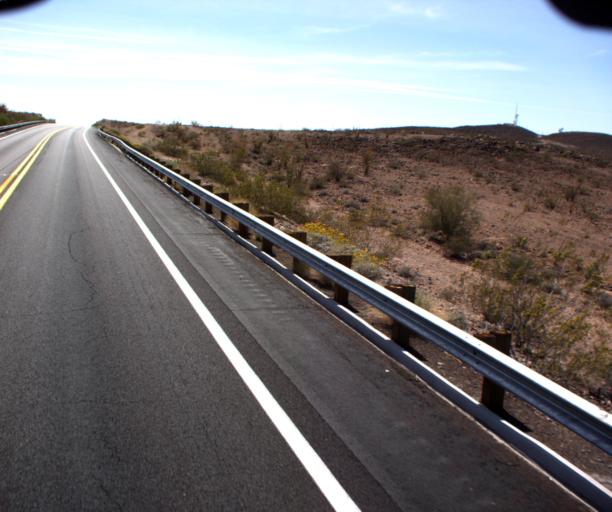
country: US
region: Arizona
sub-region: La Paz County
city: Quartzsite
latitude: 33.2476
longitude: -114.2475
